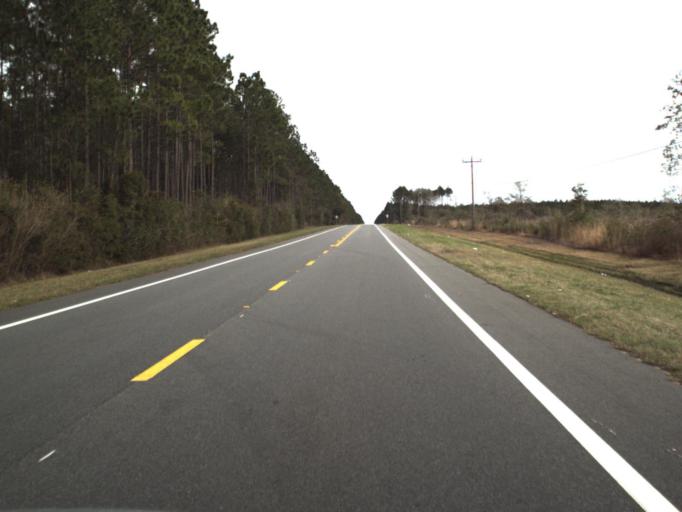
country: US
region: Florida
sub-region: Bay County
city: Callaway
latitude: 30.1479
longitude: -85.4570
